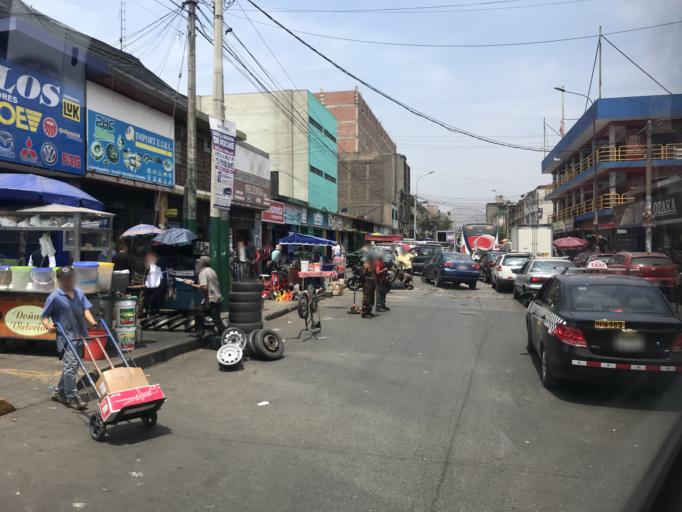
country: PE
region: Lima
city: Lima
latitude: -12.0607
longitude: -77.0312
